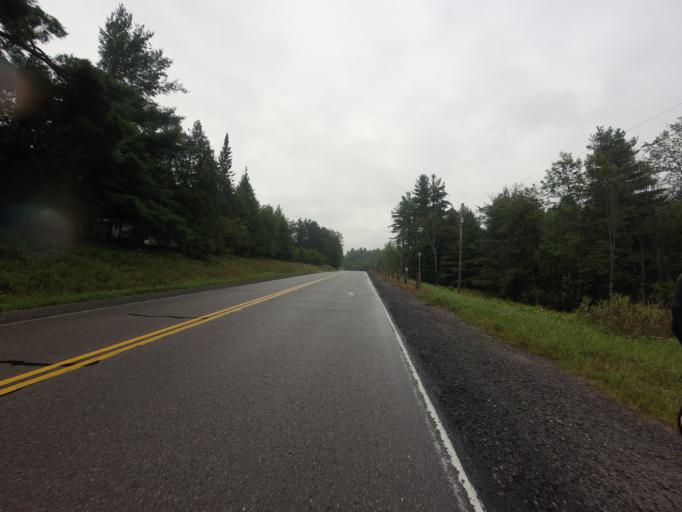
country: CA
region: Ontario
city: Perth
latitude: 45.0892
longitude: -76.4098
